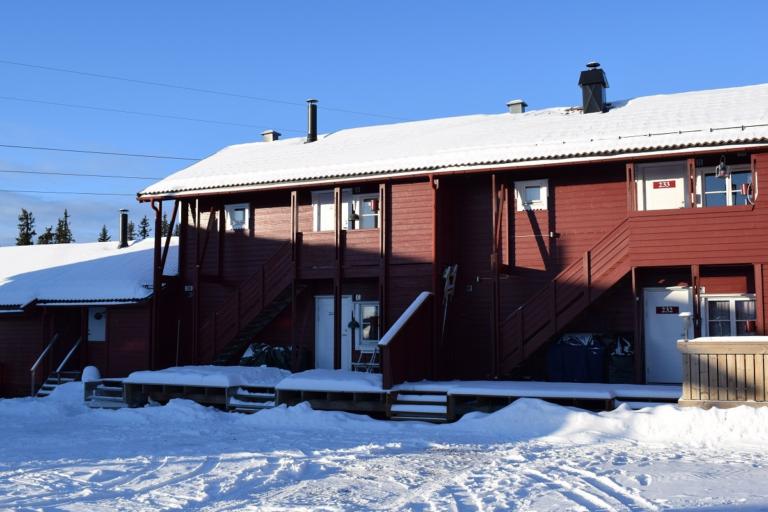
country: NO
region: Oppland
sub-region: Gausdal
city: Segalstad bru
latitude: 61.3330
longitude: 10.0884
